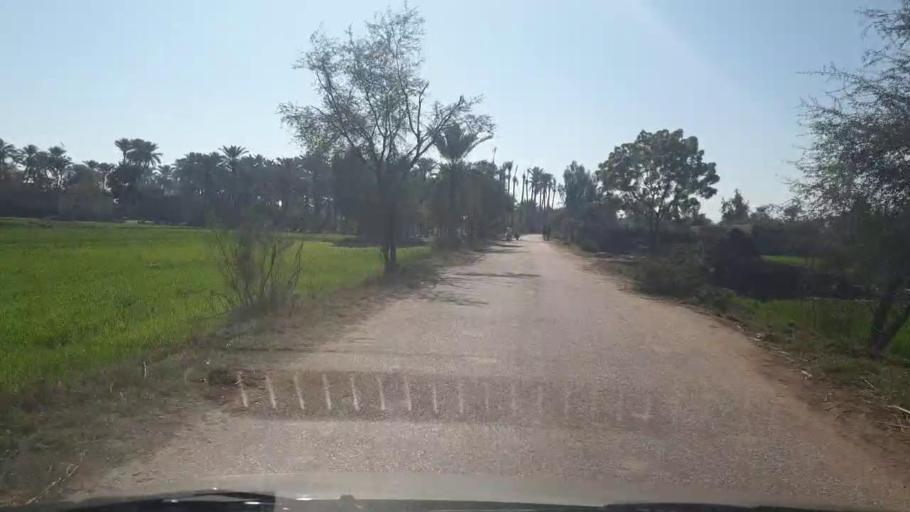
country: PK
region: Sindh
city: Bozdar
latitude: 27.1395
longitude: 68.6451
